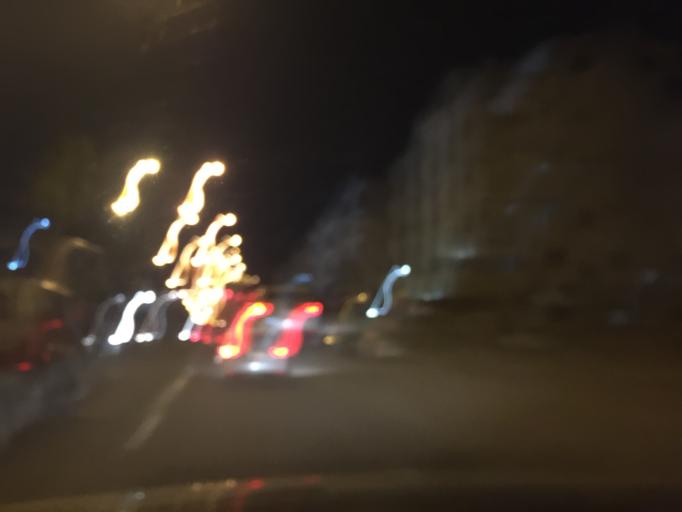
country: JO
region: Amman
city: Amman
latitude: 31.9914
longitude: 35.9297
